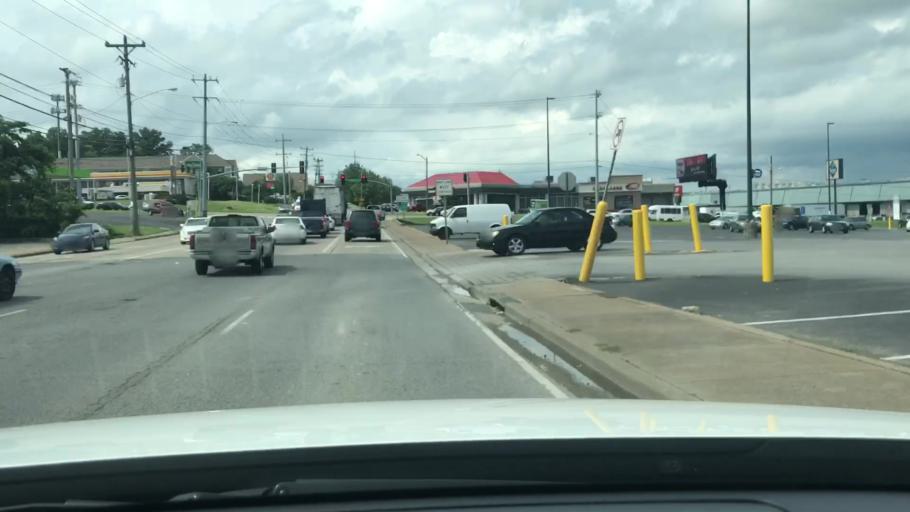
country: US
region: Tennessee
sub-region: Davidson County
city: Oak Hill
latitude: 36.0864
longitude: -86.6913
